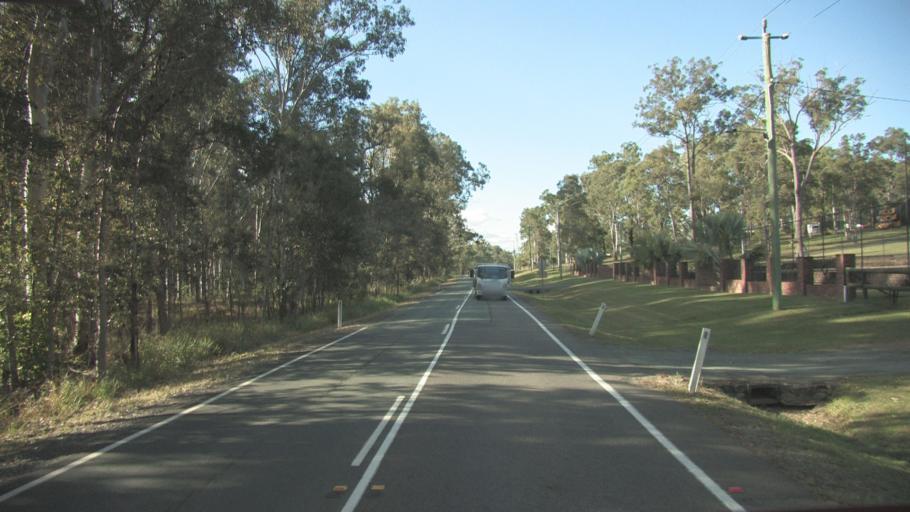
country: AU
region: Queensland
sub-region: Ipswich
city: Springfield Lakes
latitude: -27.7264
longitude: 152.9562
